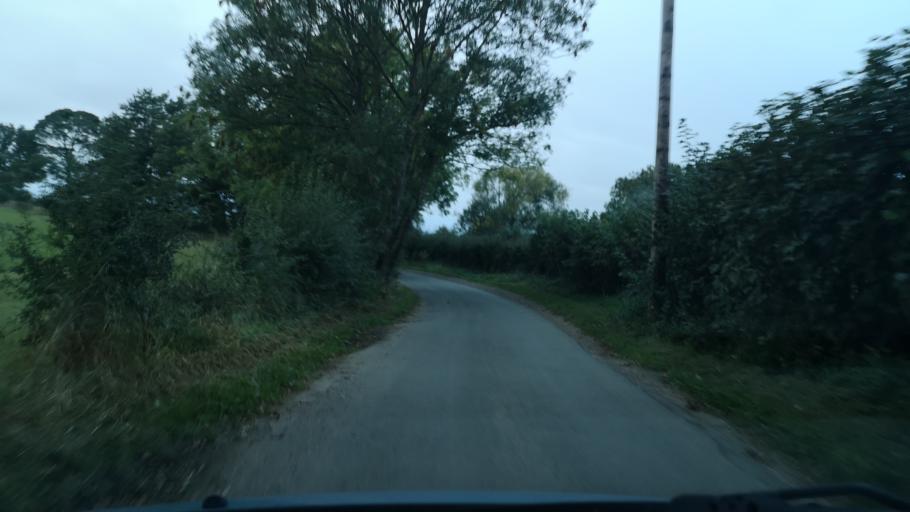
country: GB
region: England
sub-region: City and Borough of Wakefield
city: Low Ackworth
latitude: 53.6587
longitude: -1.3183
